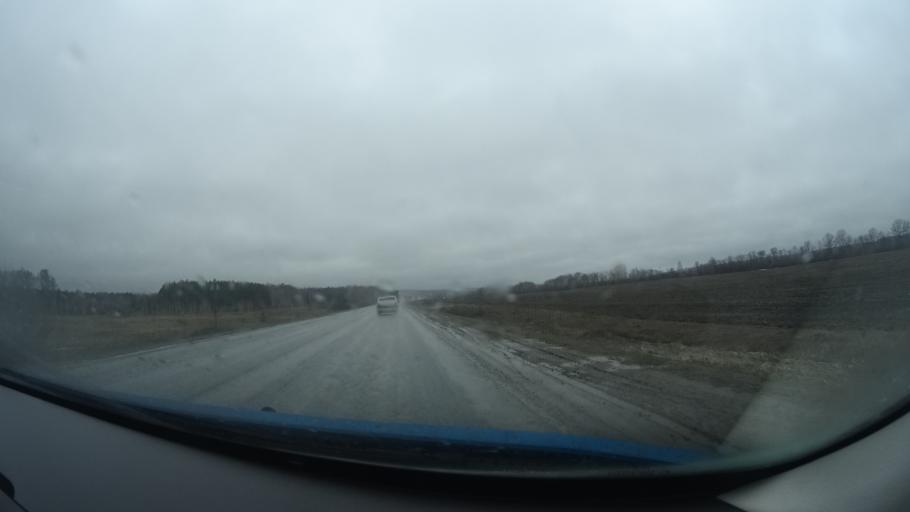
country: RU
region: Bashkortostan
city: Kandry
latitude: 54.6120
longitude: 54.3187
